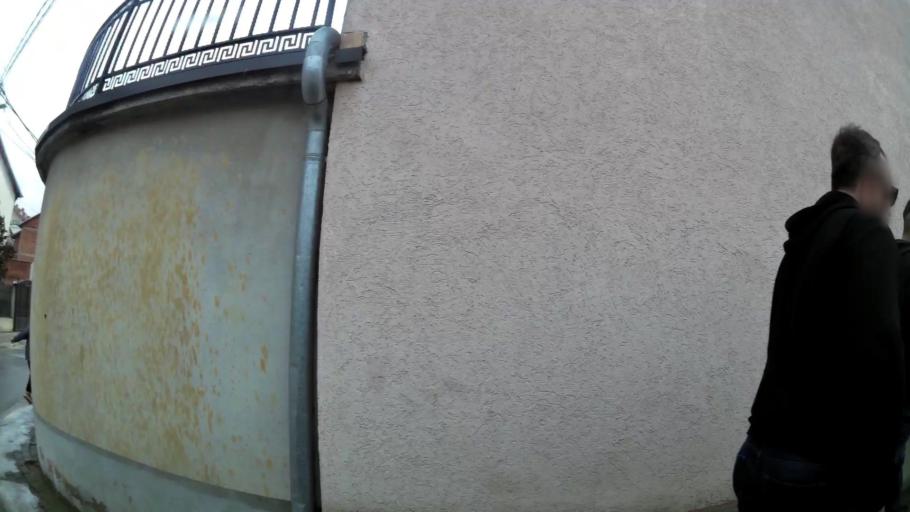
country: XK
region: Pristina
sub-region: Komuna e Prishtines
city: Pristina
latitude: 42.6809
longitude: 21.1634
